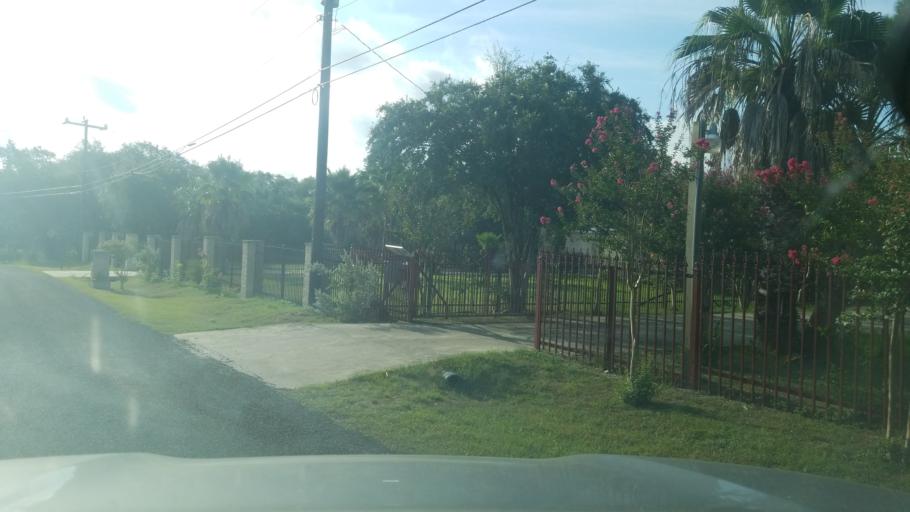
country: US
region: Texas
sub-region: Bexar County
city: Timberwood Park
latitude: 29.6971
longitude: -98.5180
